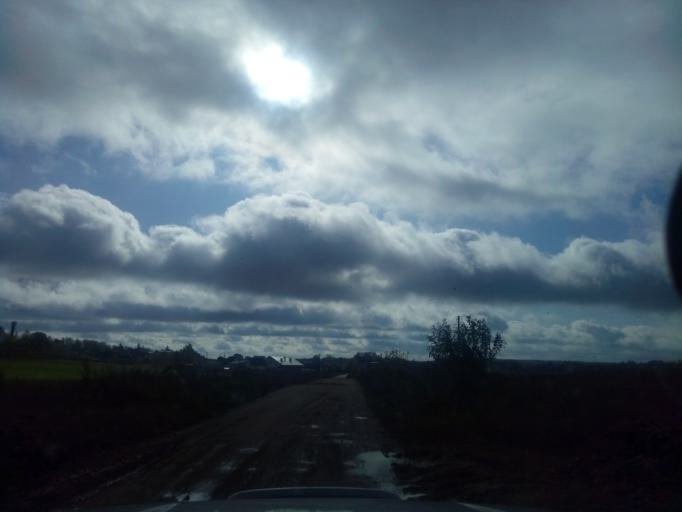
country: BY
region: Minsk
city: Zaslawye
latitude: 54.0201
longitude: 27.2900
